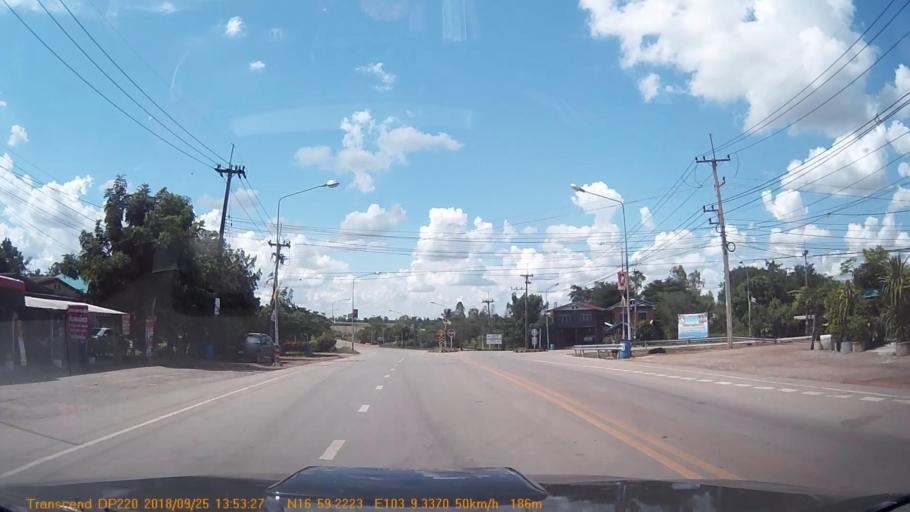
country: TH
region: Changwat Udon Thani
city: Si That
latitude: 16.9870
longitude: 103.1556
